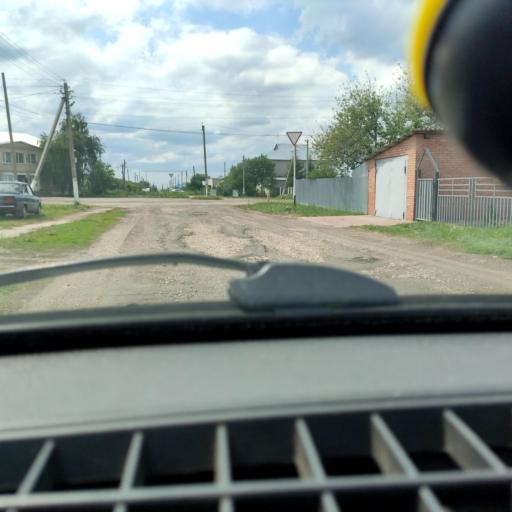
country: RU
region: Samara
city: Povolzhskiy
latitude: 53.6467
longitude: 49.6890
